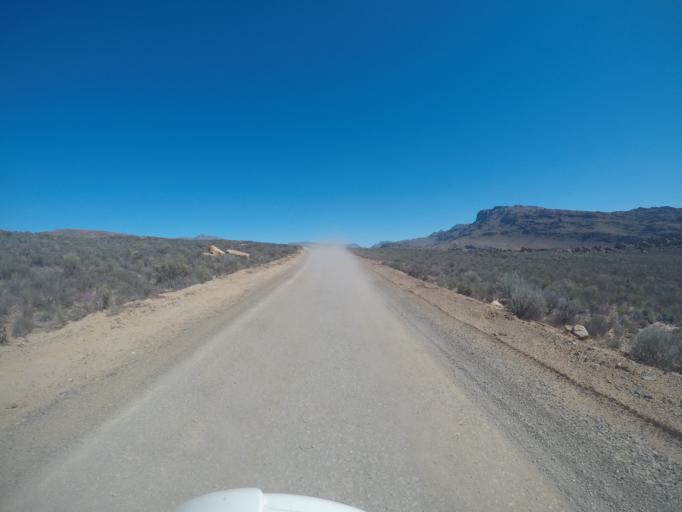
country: ZA
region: Western Cape
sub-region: West Coast District Municipality
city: Clanwilliam
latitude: -32.5073
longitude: 19.3057
